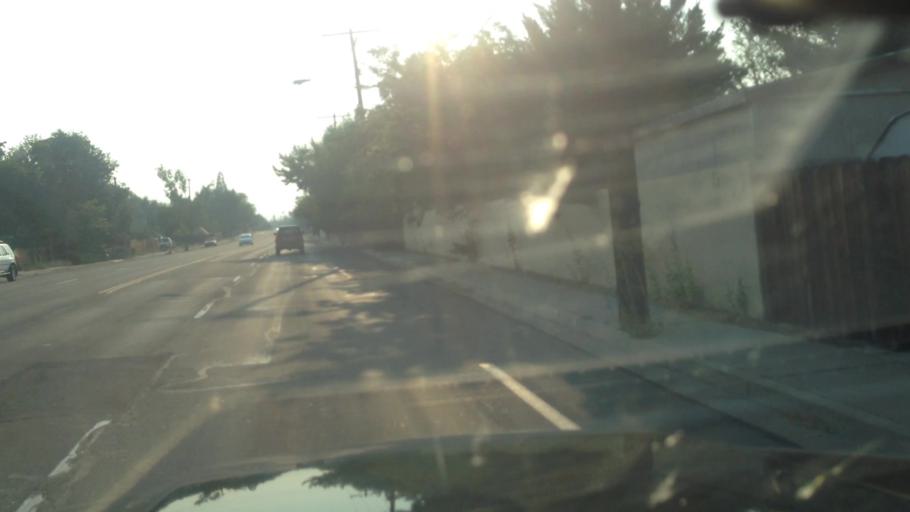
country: US
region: Nevada
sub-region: Washoe County
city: Reno
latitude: 39.5055
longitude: -119.8190
